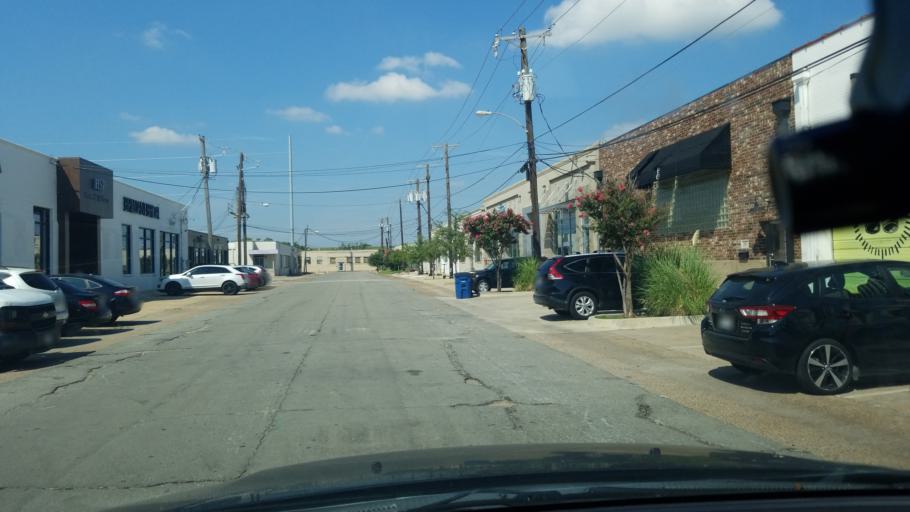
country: US
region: Texas
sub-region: Dallas County
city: Dallas
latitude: 32.7874
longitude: -96.8201
